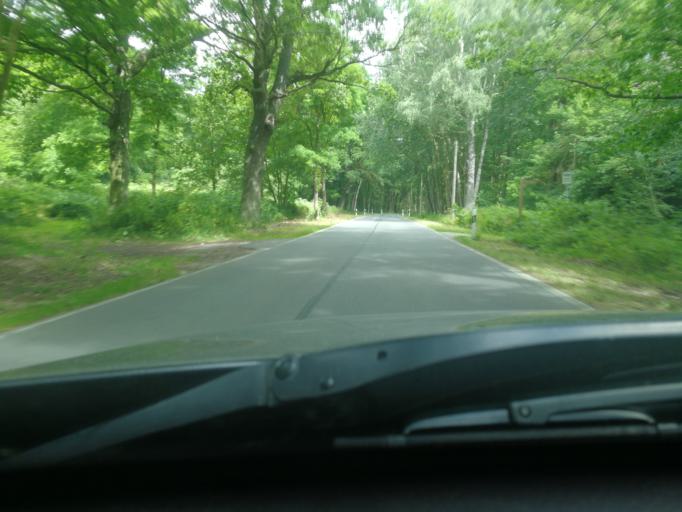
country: DE
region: Mecklenburg-Vorpommern
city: Prohn
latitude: 54.4248
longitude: 13.0234
